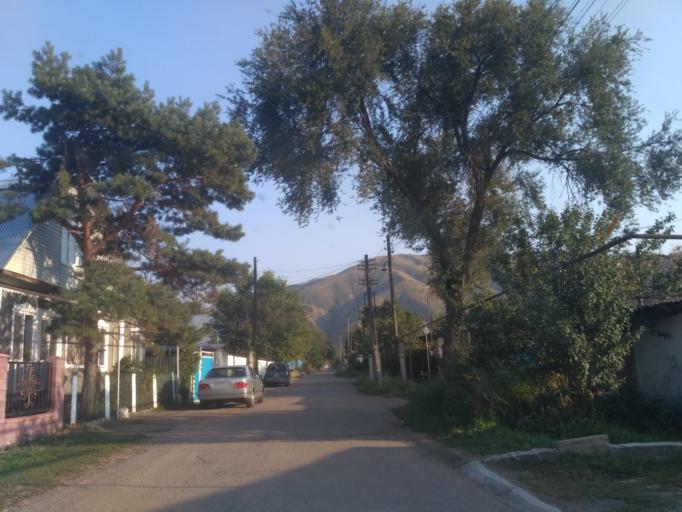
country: KZ
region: Almaty Oblysy
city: Burunday
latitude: 43.1655
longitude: 76.4043
